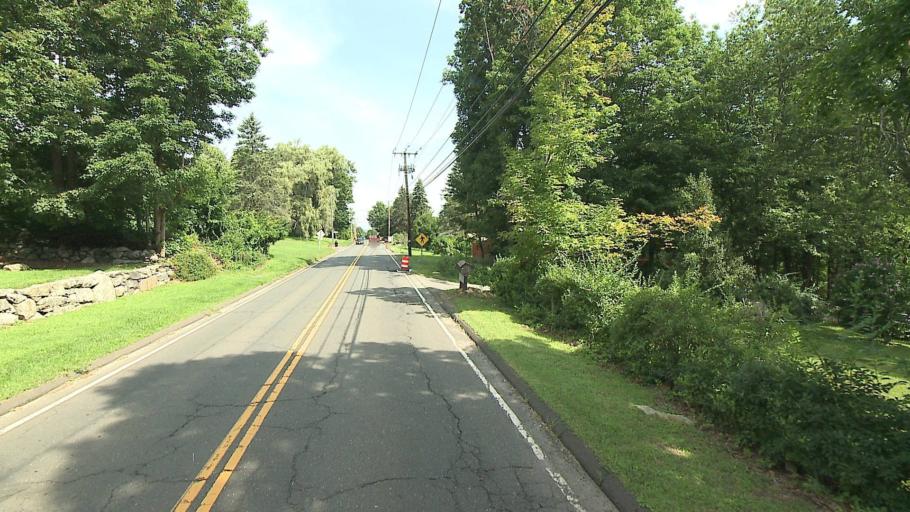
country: US
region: New York
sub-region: Putnam County
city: Putnam Lake
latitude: 41.4525
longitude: -73.5235
